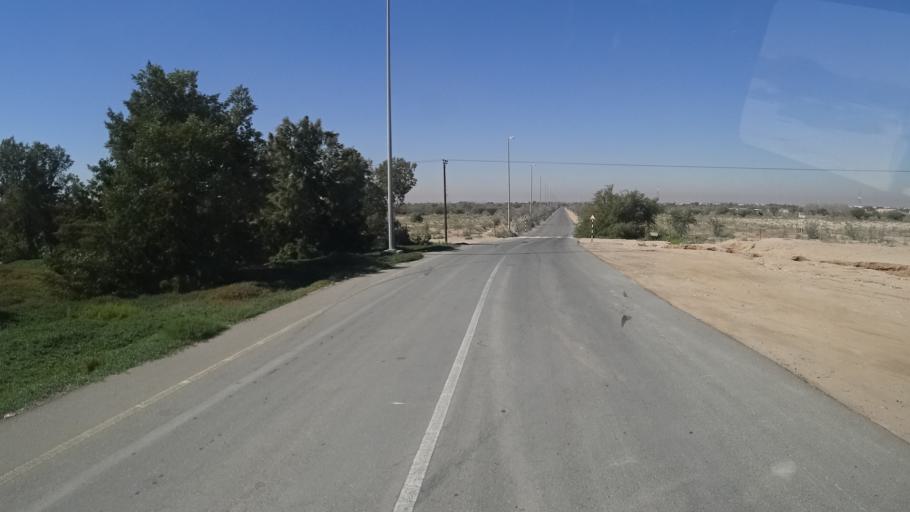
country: AE
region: Abu Dhabi
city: Al Ain
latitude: 24.1036
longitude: 55.7343
